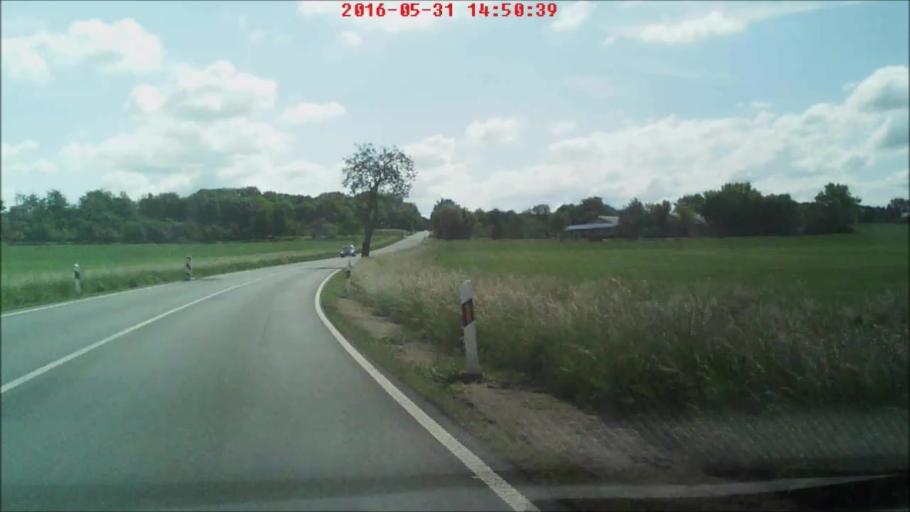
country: DE
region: Thuringia
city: Gunstedt
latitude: 51.2111
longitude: 11.0728
